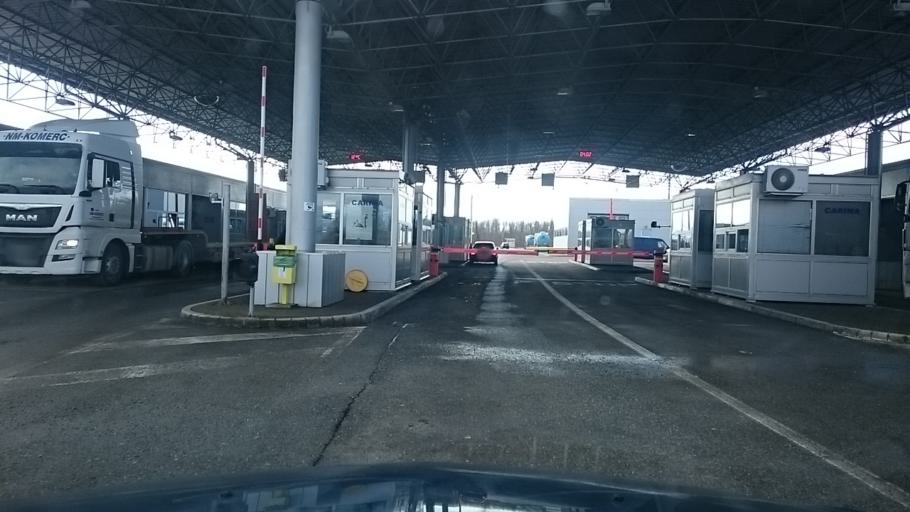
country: HR
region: Sisacko-Moslavacka
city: Novska
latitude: 45.2657
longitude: 16.9190
